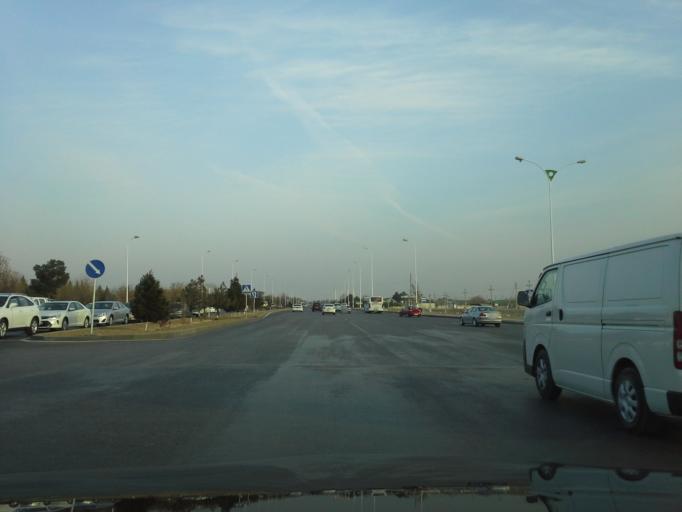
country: TM
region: Ahal
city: Abadan
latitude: 38.0339
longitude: 58.2238
